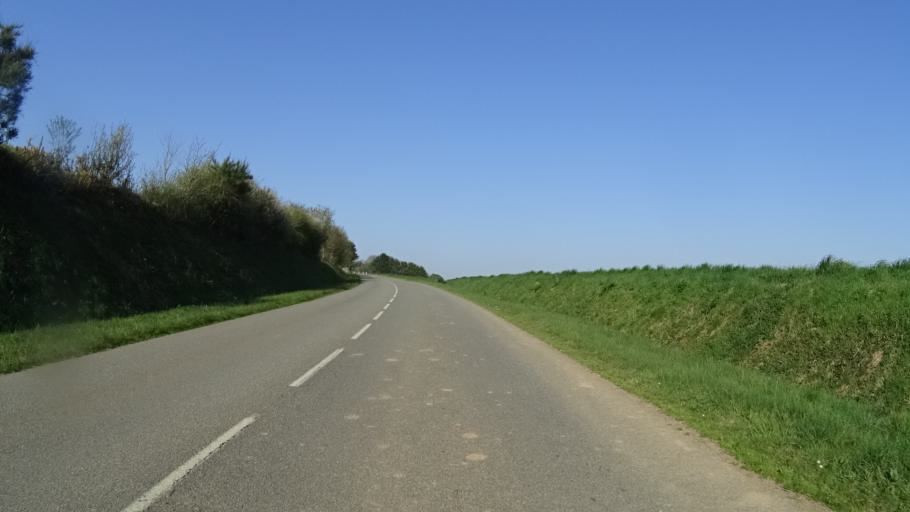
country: FR
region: Brittany
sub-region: Departement du Finistere
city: Irvillac
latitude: 48.3616
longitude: -4.2330
